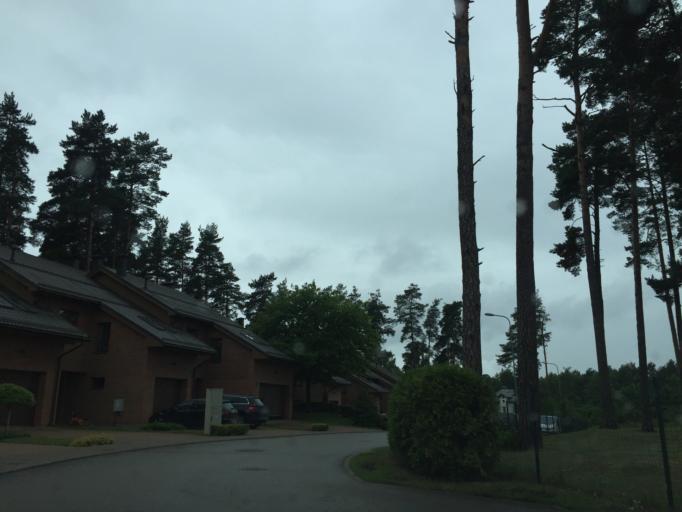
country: LV
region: Riga
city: Jaunciems
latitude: 57.0174
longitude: 24.2157
